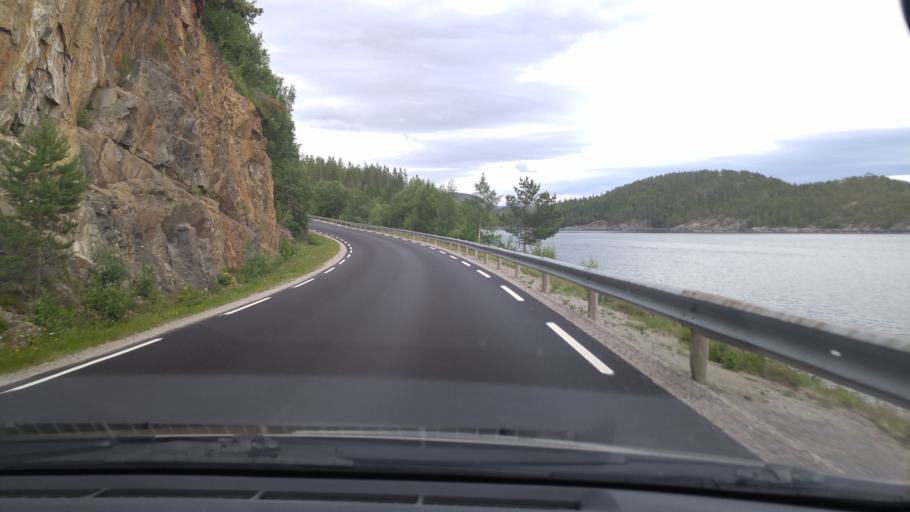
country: NO
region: Nord-Trondelag
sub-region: Namsos
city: Namsos
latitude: 64.5502
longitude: 11.4768
